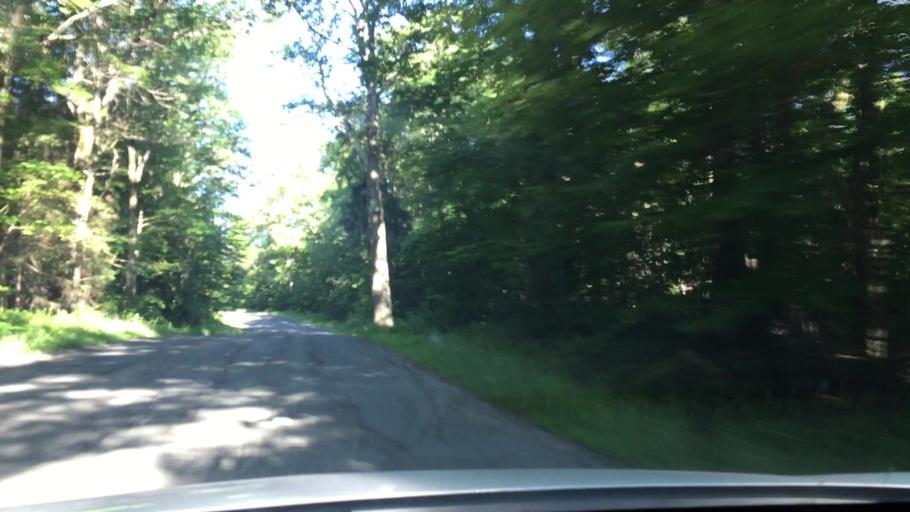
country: US
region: Massachusetts
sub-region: Berkshire County
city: Becket
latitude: 42.2997
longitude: -73.1401
